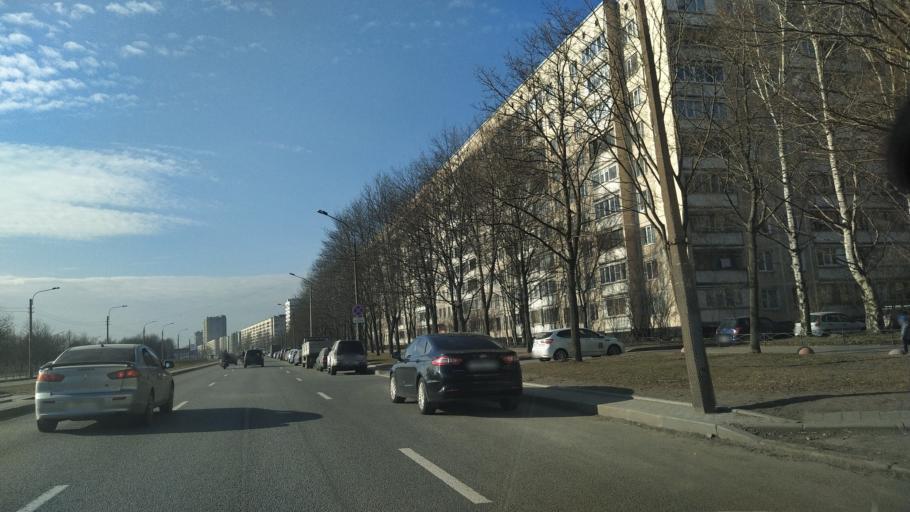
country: RU
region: St.-Petersburg
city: Grazhdanka
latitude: 60.0291
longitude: 30.3984
